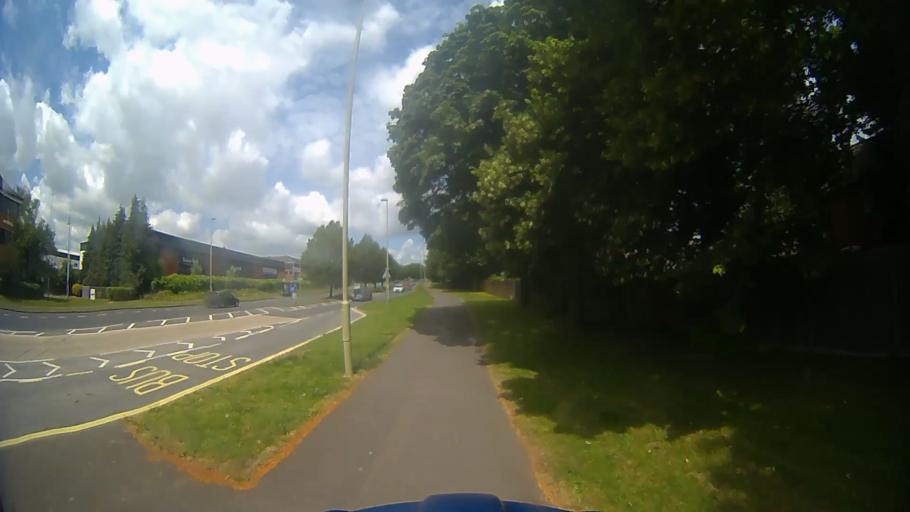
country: GB
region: England
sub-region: Hampshire
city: Andover
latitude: 51.2198
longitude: -1.4770
